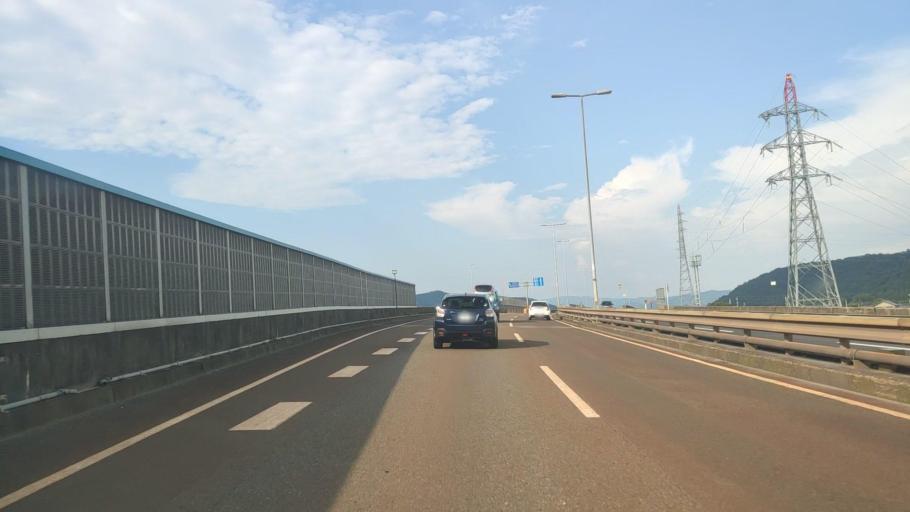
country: JP
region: Fukui
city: Takefu
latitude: 35.8749
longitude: 136.1621
